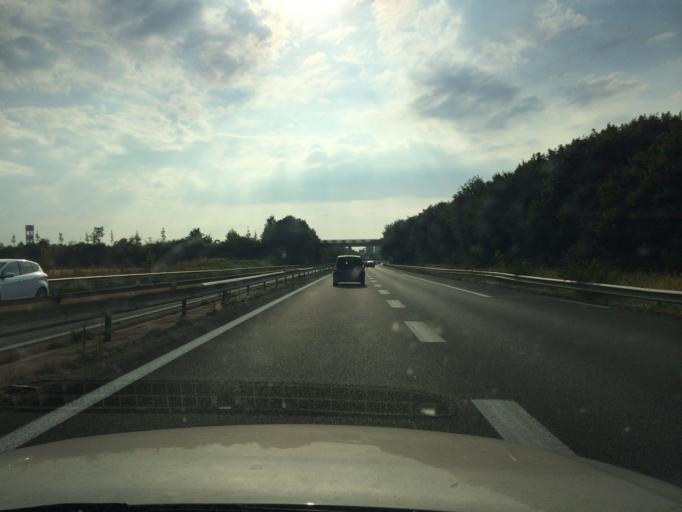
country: FR
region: Lower Normandy
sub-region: Departement du Calvados
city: Giberville
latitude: 49.1671
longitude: -0.2868
